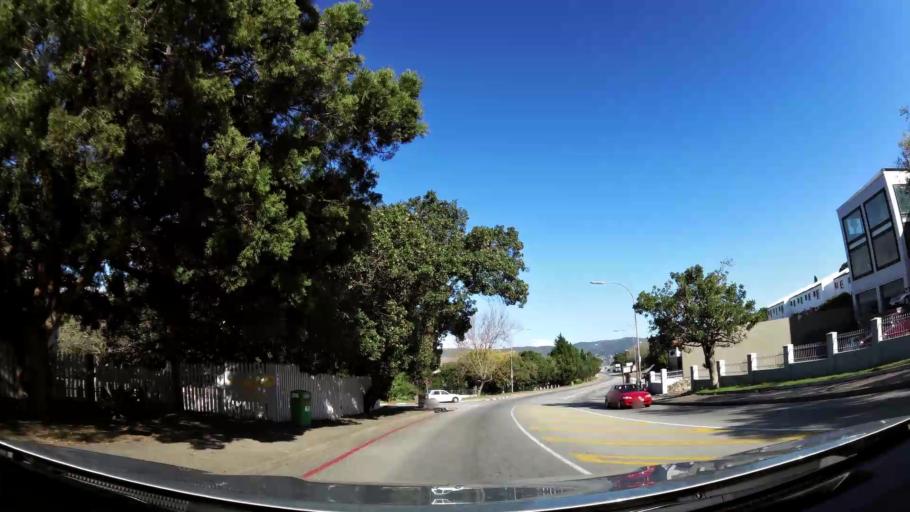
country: ZA
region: Western Cape
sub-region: Eden District Municipality
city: Knysna
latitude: -34.0362
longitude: 23.0414
